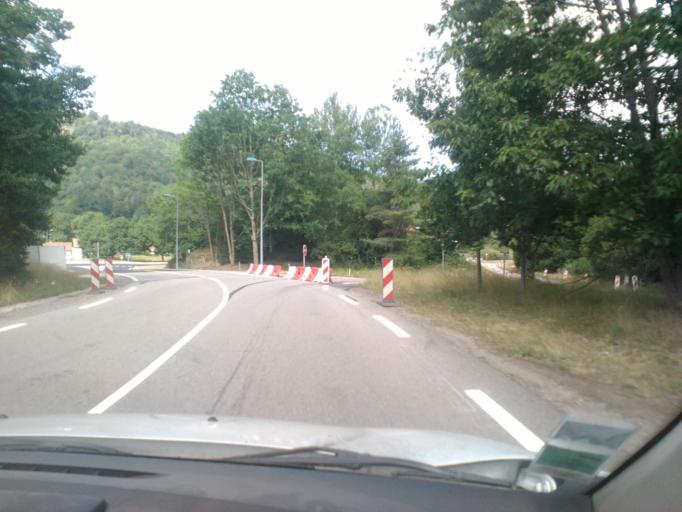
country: FR
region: Lorraine
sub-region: Departement des Vosges
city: Saulxures-sur-Moselotte
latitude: 47.9559
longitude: 6.7461
